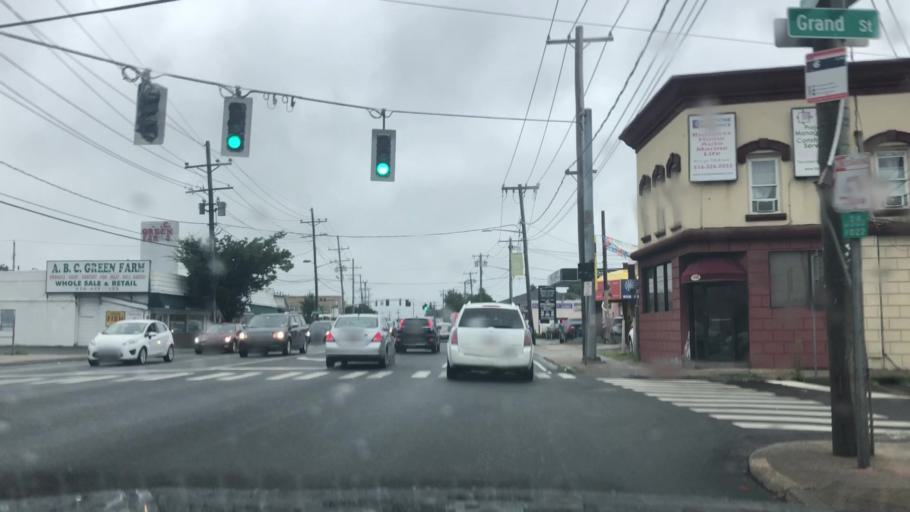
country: US
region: New York
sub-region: Nassau County
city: Stewart Manor
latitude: 40.7085
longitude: -73.6869
